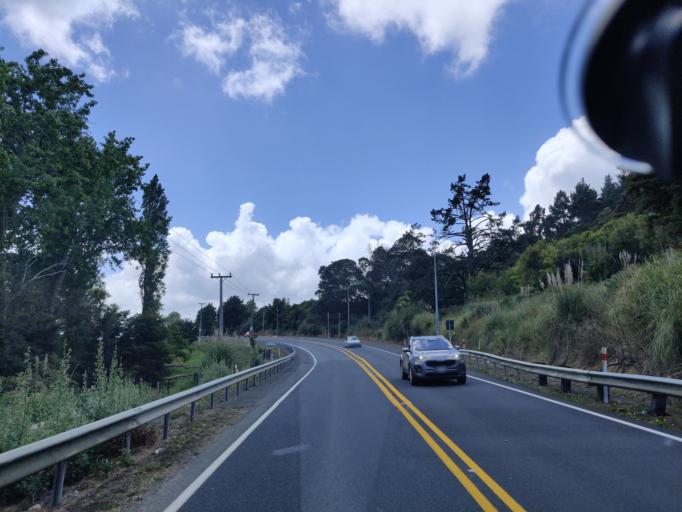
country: NZ
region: Auckland
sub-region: Auckland
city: Wellsford
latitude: -36.2512
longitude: 174.5091
